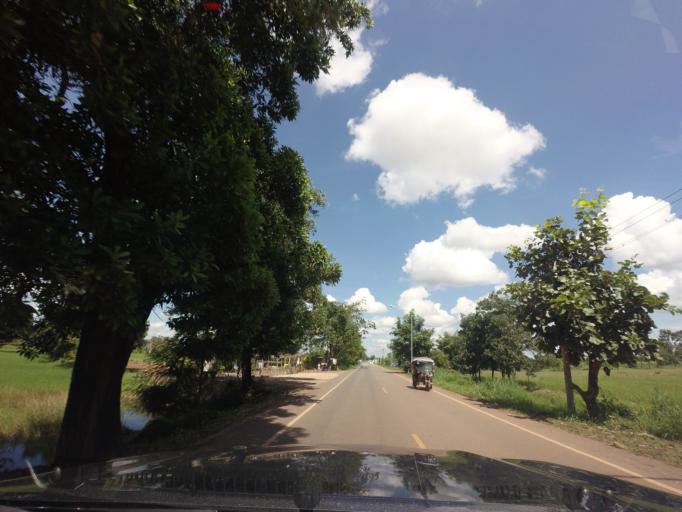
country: TH
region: Changwat Udon Thani
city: Ban Dung
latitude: 17.7390
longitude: 103.3477
